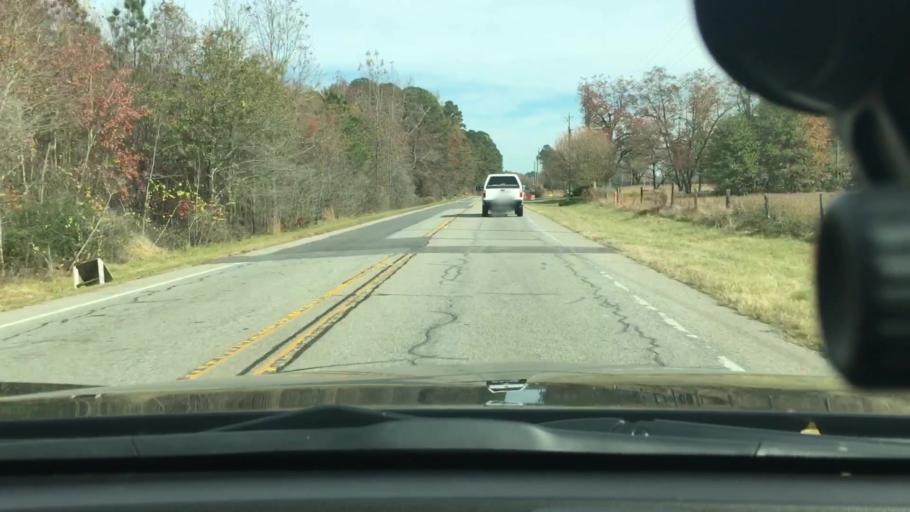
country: US
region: North Carolina
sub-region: Moore County
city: Carthage
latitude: 35.3790
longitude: -79.2862
